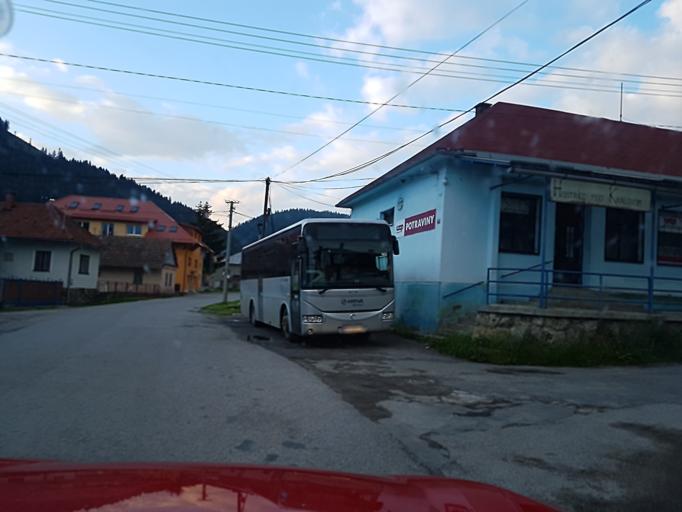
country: SK
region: Zilinsky
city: Ruzomberok
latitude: 49.1252
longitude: 19.4143
